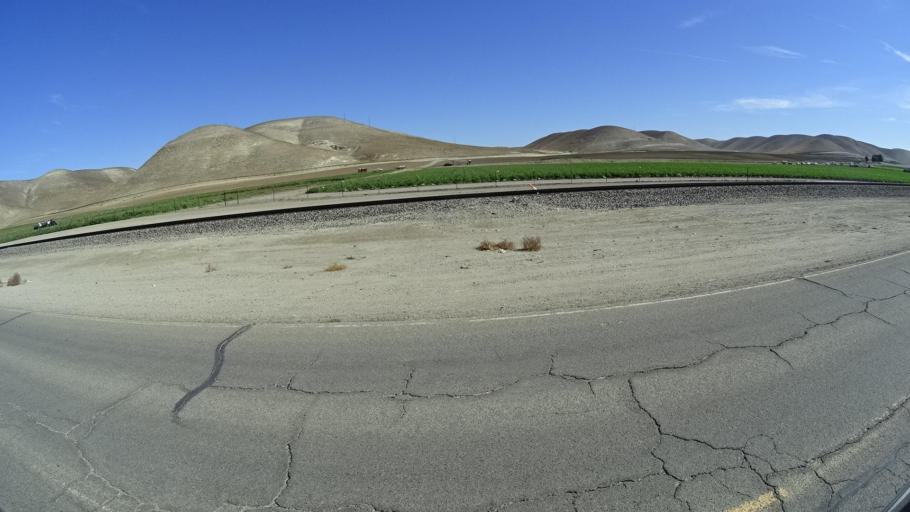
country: US
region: California
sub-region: Monterey County
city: King City
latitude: 36.0972
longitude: -120.9681
